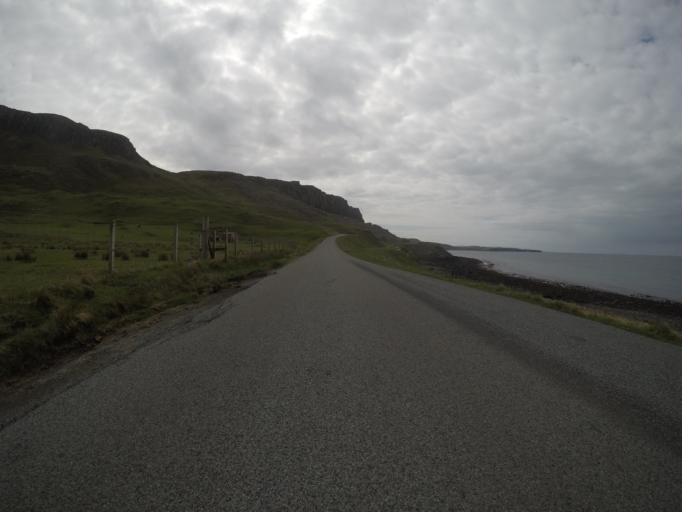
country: GB
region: Scotland
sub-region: Highland
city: Portree
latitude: 57.6775
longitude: -6.3463
